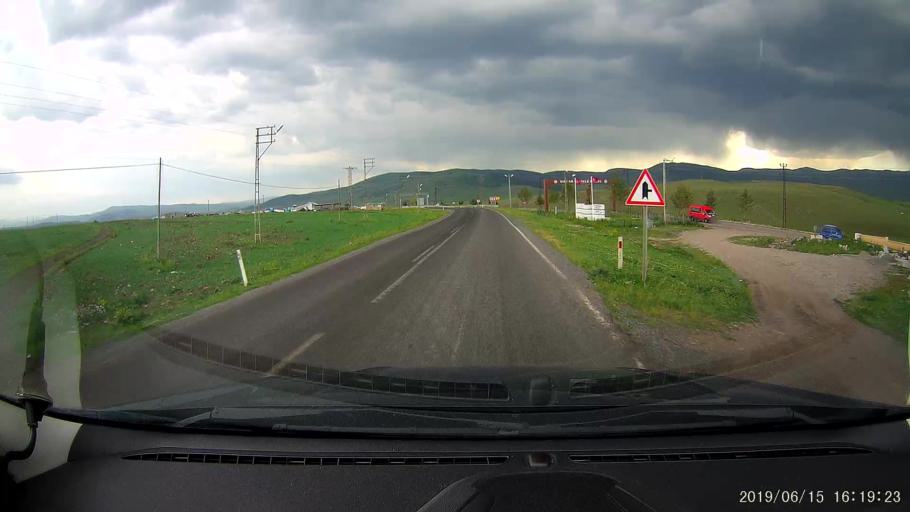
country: TR
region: Ardahan
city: Hanak
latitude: 41.2291
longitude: 42.8506
